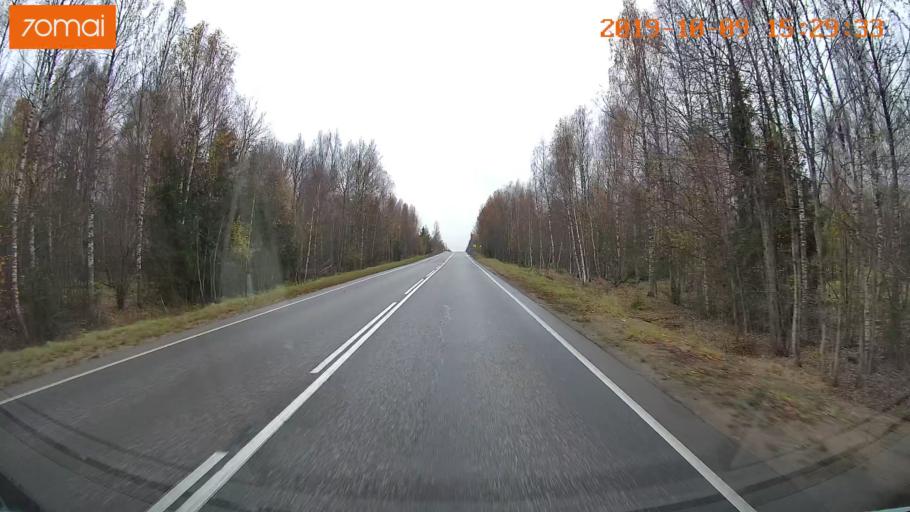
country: RU
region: Kostroma
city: Susanino
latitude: 57.9897
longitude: 41.3403
